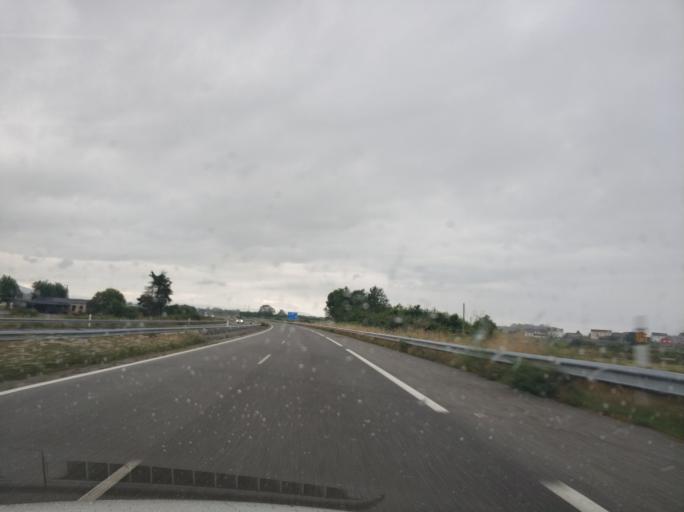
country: ES
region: Asturias
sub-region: Province of Asturias
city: Figueras
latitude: 43.5440
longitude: -7.0025
